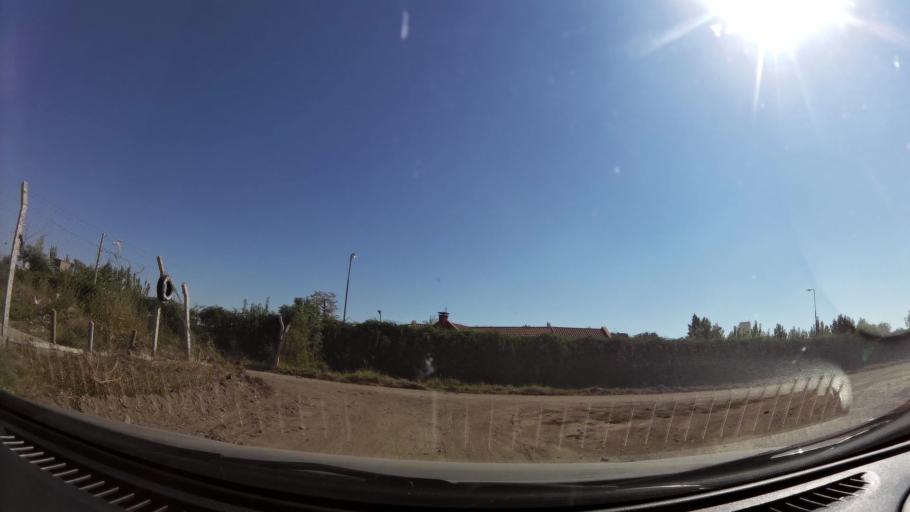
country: AR
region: Cordoba
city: Villa Allende
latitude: -31.3087
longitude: -64.2535
